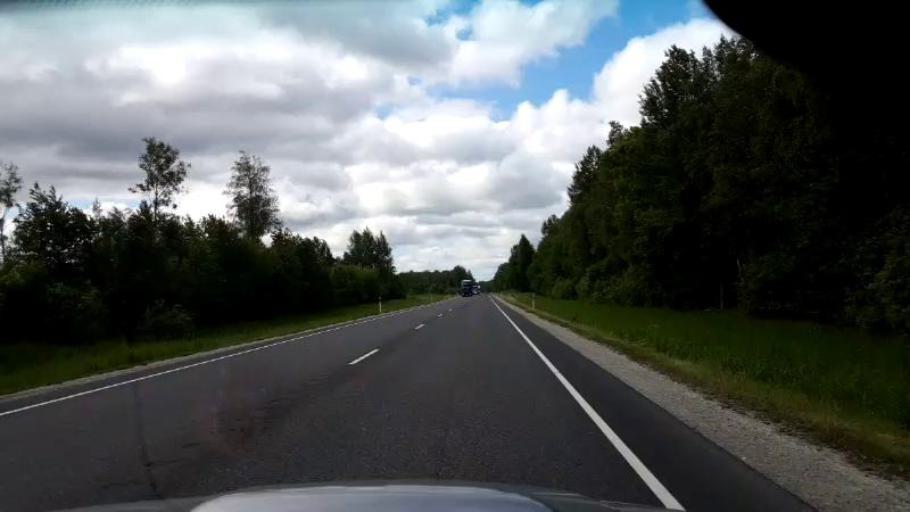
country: EE
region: Raplamaa
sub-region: Maerjamaa vald
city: Marjamaa
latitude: 58.8345
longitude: 24.4202
